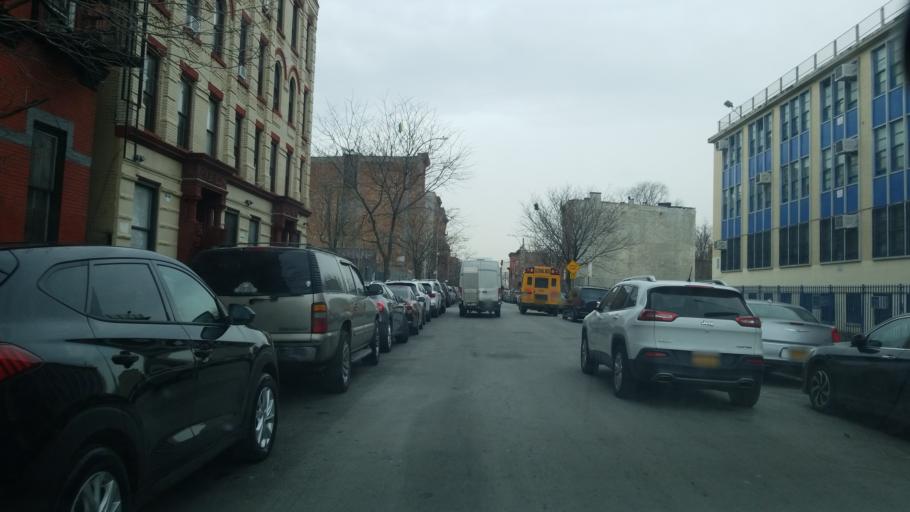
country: US
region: New York
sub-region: New York County
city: Manhattan
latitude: 40.8099
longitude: -73.9226
